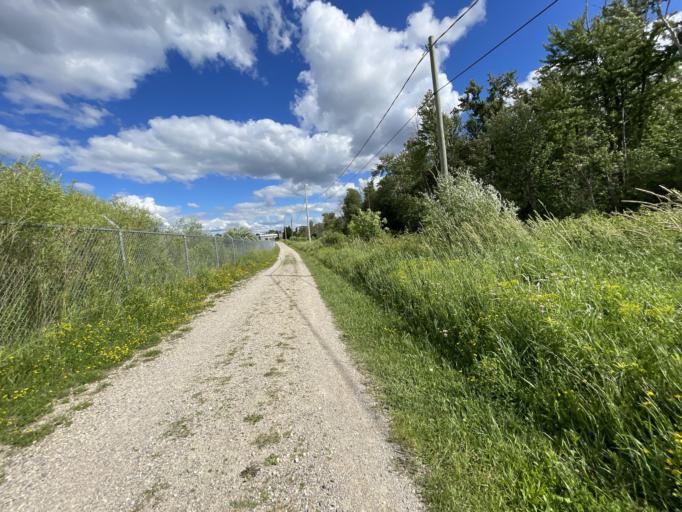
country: CA
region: Ontario
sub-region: Wellington County
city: Guelph
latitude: 43.5764
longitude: -80.2361
